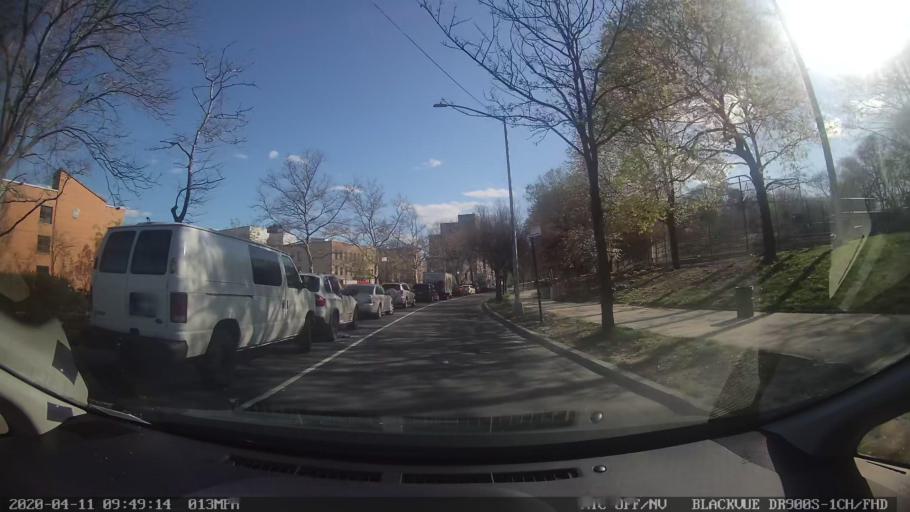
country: US
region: New York
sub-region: New York County
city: Inwood
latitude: 40.8409
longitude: -73.9052
